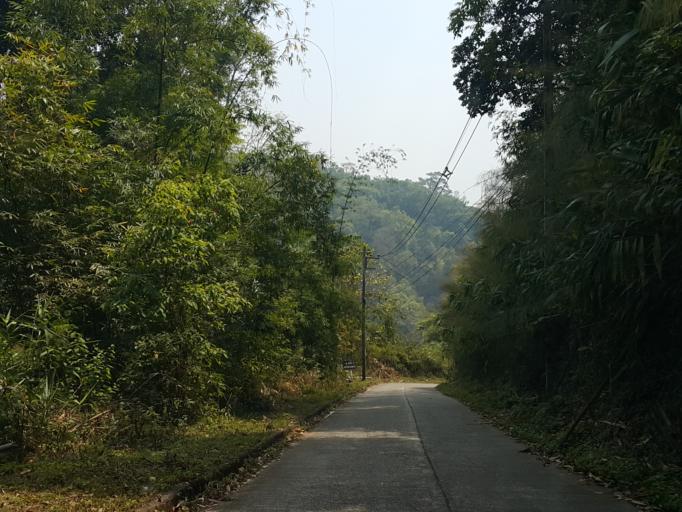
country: TH
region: Lampang
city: Mueang Pan
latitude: 18.8290
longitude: 99.4226
